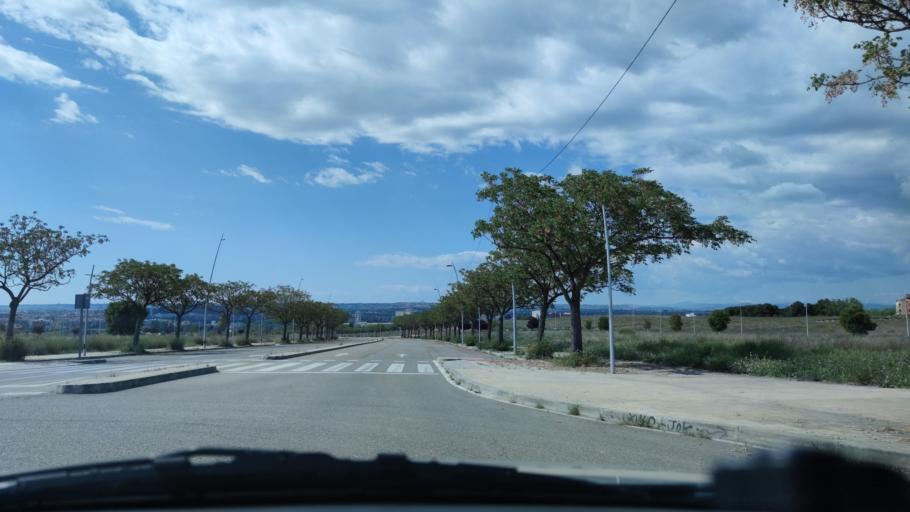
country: ES
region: Catalonia
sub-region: Provincia de Lleida
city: Lleida
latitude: 41.6030
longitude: 0.6633
